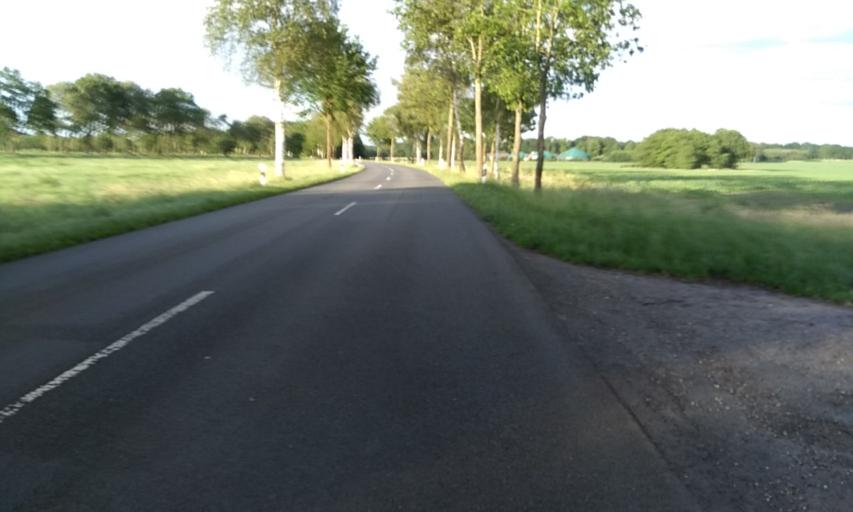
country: DE
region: Lower Saxony
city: Anderlingen
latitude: 53.3861
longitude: 9.3163
